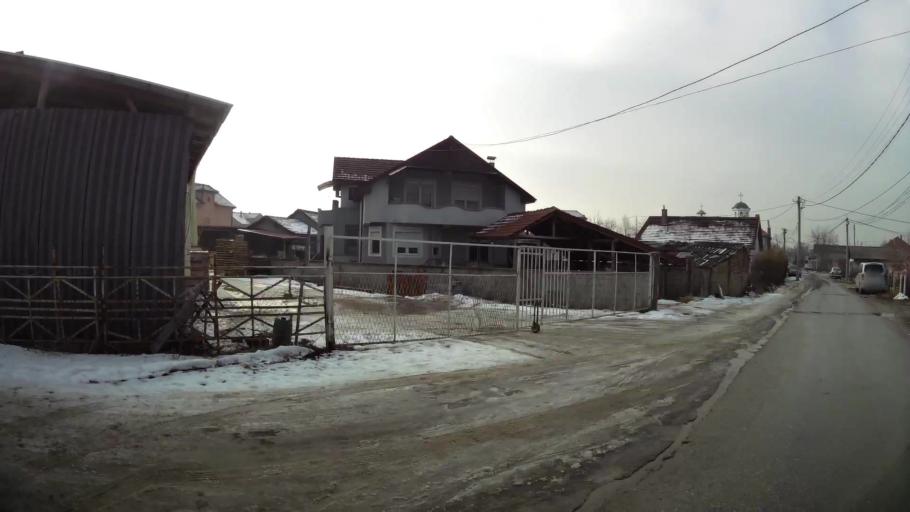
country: MK
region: Ilinden
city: Marino
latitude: 41.9948
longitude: 21.5895
